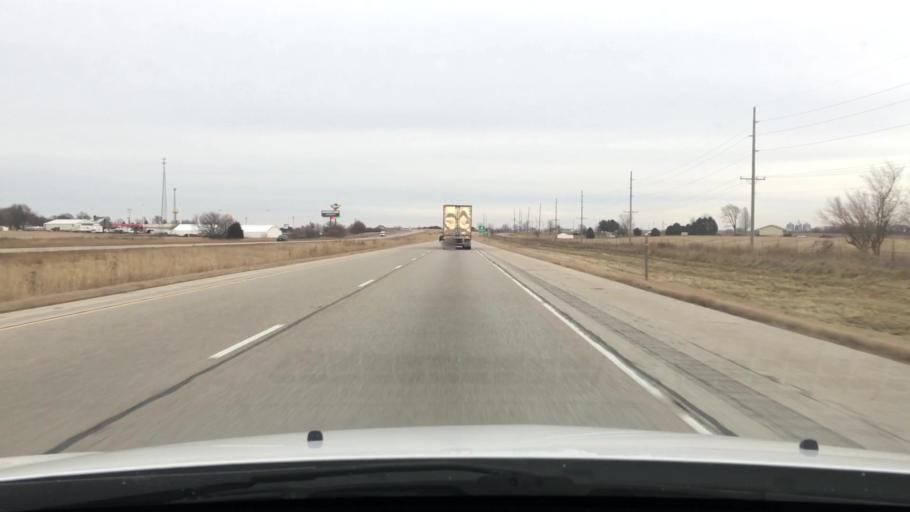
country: US
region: Illinois
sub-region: Logan County
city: Atlanta
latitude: 40.3057
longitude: -89.1751
